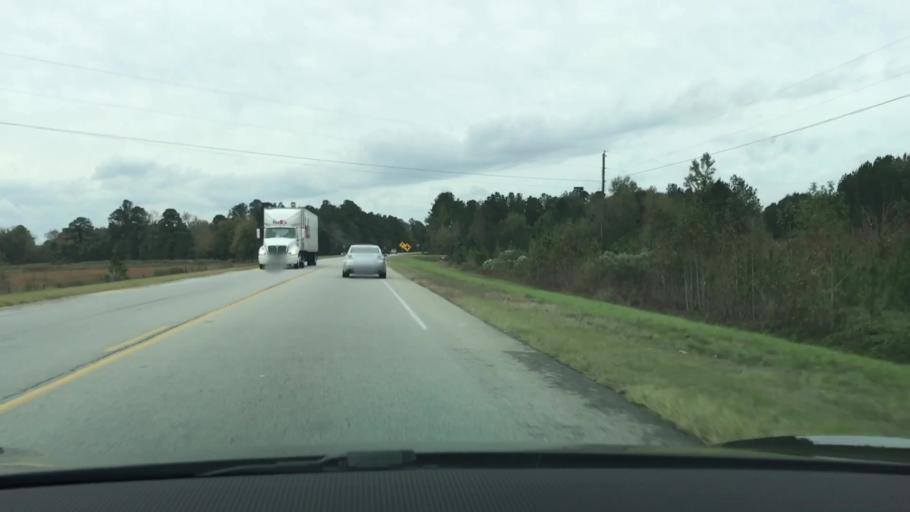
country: US
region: Georgia
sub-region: Jefferson County
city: Louisville
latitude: 32.9650
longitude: -82.3906
